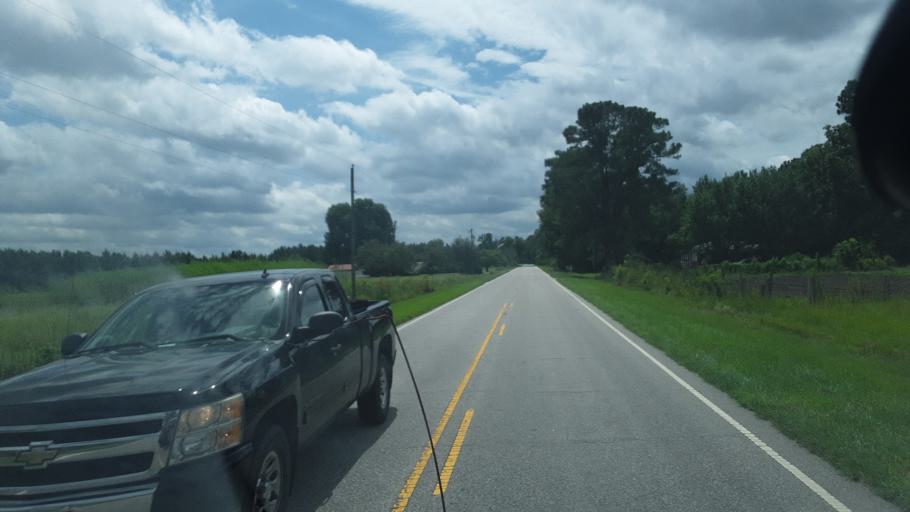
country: US
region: North Carolina
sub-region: Columbus County
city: Tabor City
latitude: 34.2854
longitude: -79.0408
